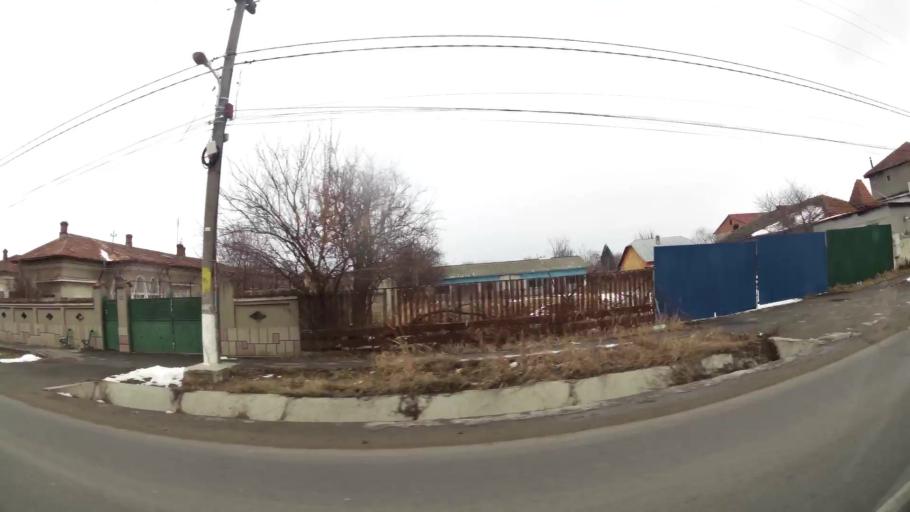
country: RO
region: Ilfov
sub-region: Comuna Afumati
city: Afumati
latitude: 44.5275
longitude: 26.2422
